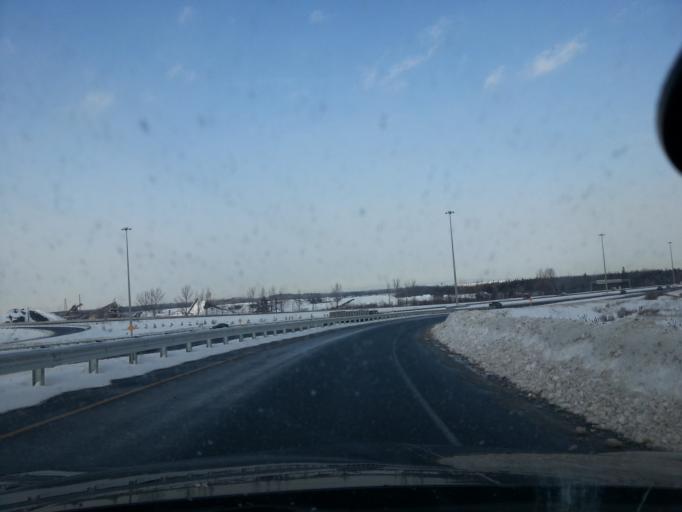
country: CA
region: Ontario
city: Bells Corners
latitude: 45.2808
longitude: -75.9555
